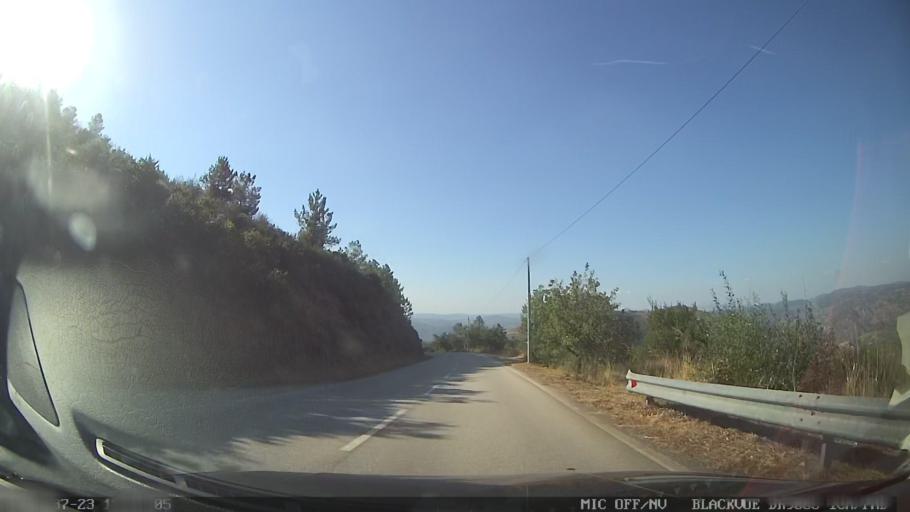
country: PT
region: Viseu
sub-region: Sao Joao da Pesqueira
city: Sao Joao da Pesqueira
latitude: 41.1655
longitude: -7.4337
